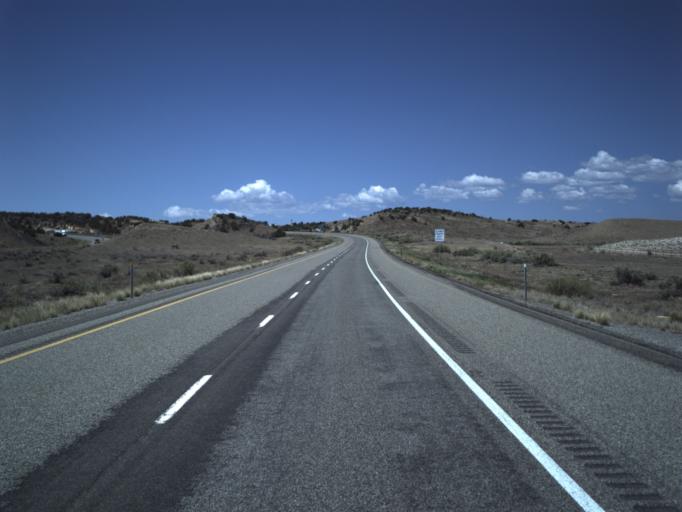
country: US
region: Colorado
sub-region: Mesa County
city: Loma
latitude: 39.1897
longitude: -109.1037
